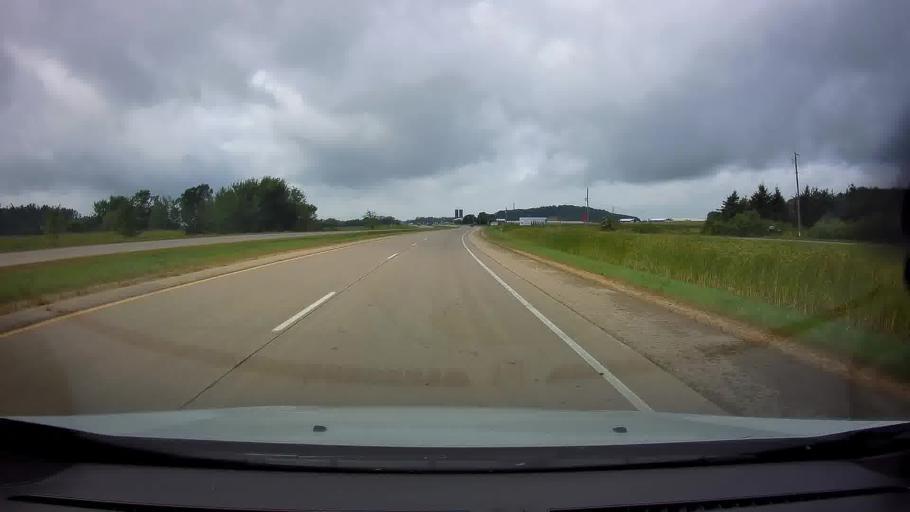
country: US
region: Wisconsin
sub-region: Shawano County
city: Shawano
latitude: 44.7967
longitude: -88.7139
